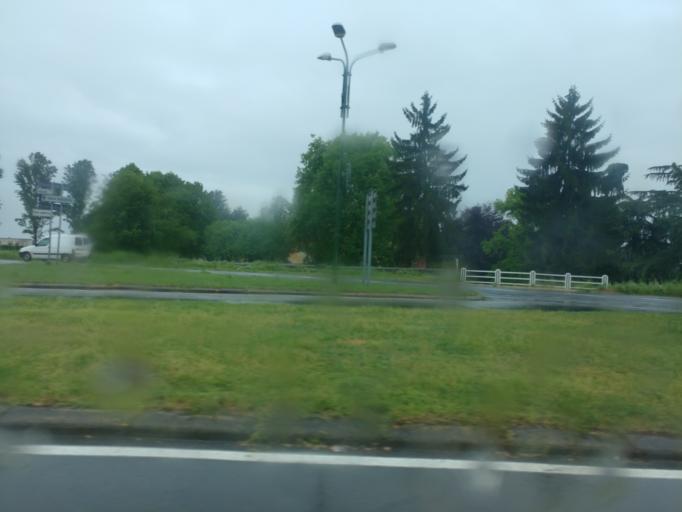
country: IT
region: Piedmont
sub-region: Provincia di Cuneo
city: Saluzzo
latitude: 44.6537
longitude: 7.4960
